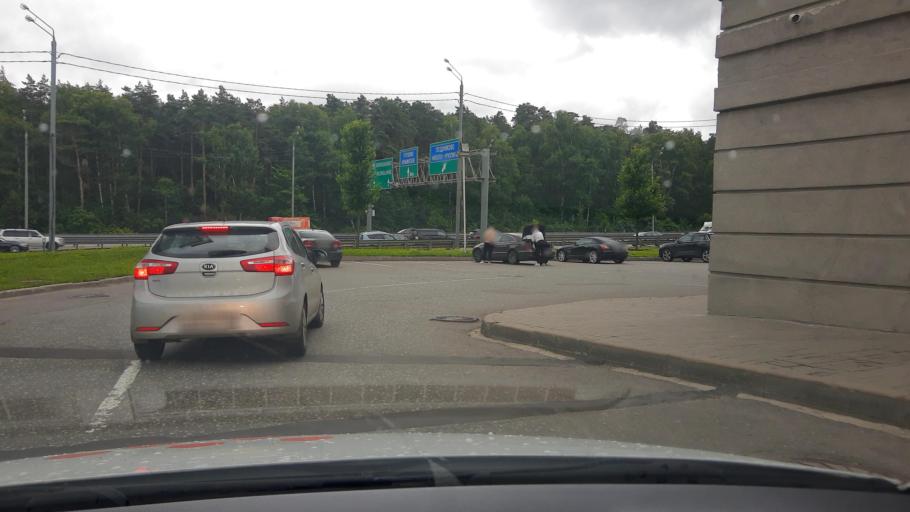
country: RU
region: Moskovskaya
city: Opalikha
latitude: 55.7864
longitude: 37.2477
